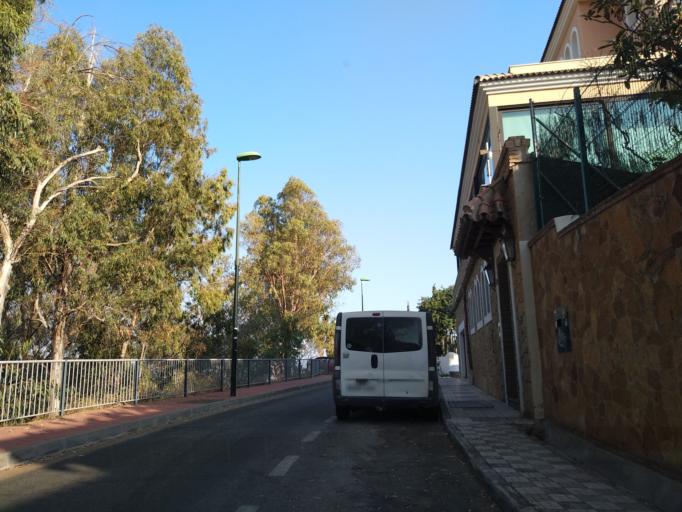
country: ES
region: Andalusia
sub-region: Provincia de Malaga
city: Malaga
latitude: 36.7326
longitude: -4.3858
